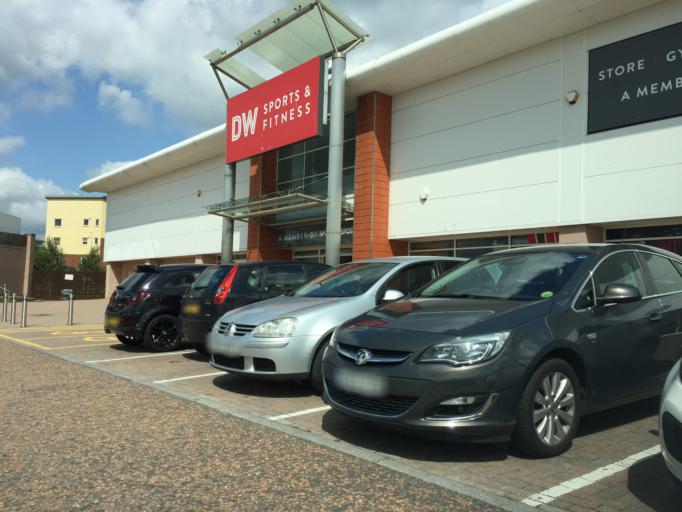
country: GB
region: England
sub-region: Gloucestershire
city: Gloucester
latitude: 51.8748
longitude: -2.2480
